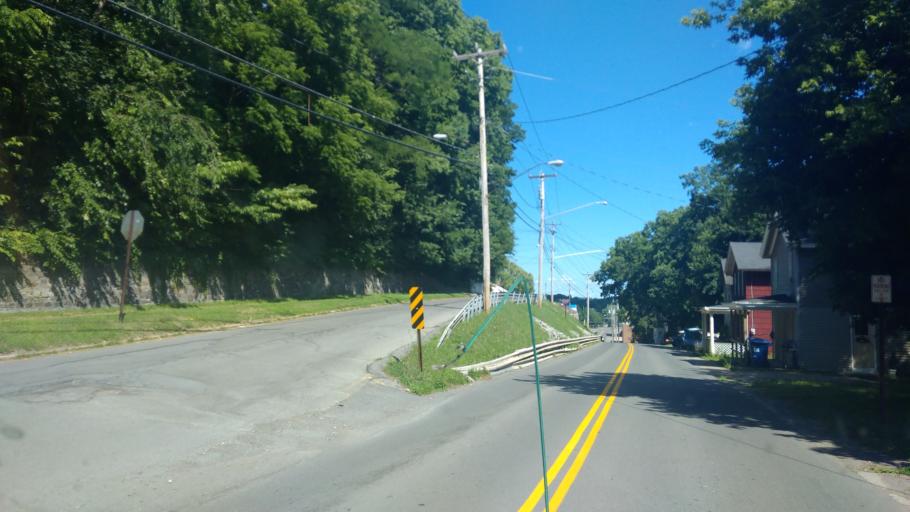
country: US
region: New York
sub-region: Wayne County
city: Lyons
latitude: 43.0636
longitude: -76.9981
